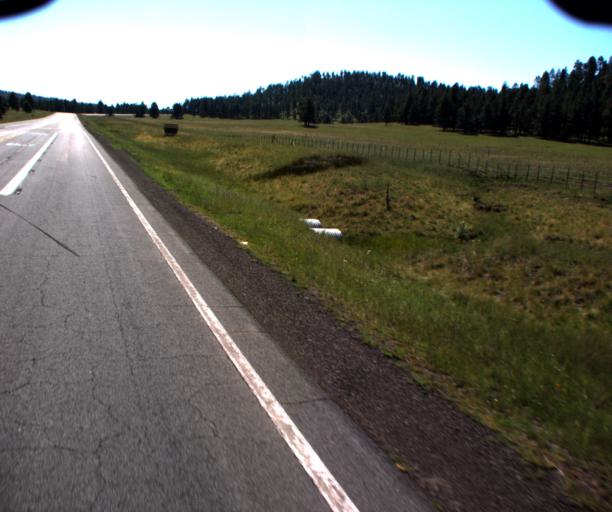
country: US
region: Arizona
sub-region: Apache County
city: Eagar
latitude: 33.8271
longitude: -109.0914
